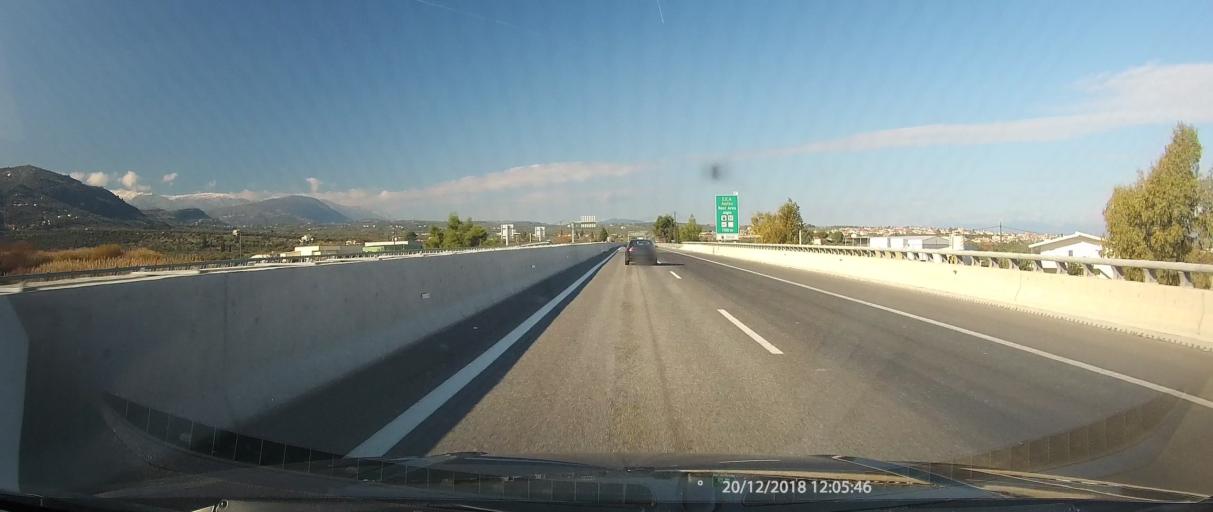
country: GR
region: West Greece
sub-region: Nomos Achaias
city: Aigio
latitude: 38.2266
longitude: 22.0922
